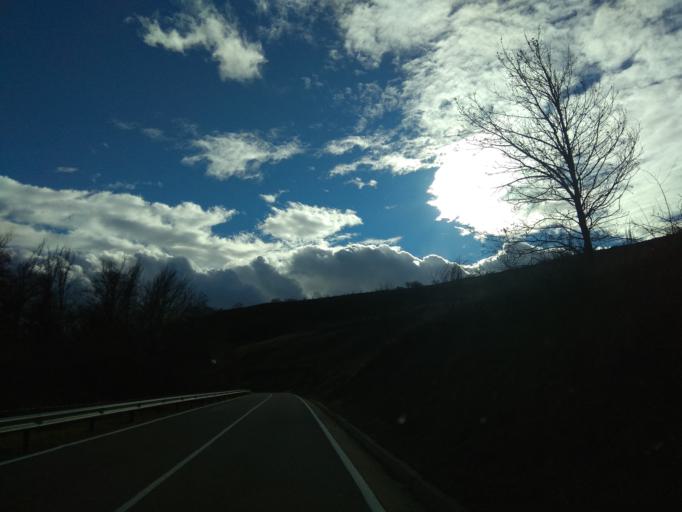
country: ES
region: Cantabria
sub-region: Provincia de Cantabria
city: San Martin de Elines
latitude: 42.8554
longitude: -3.9135
